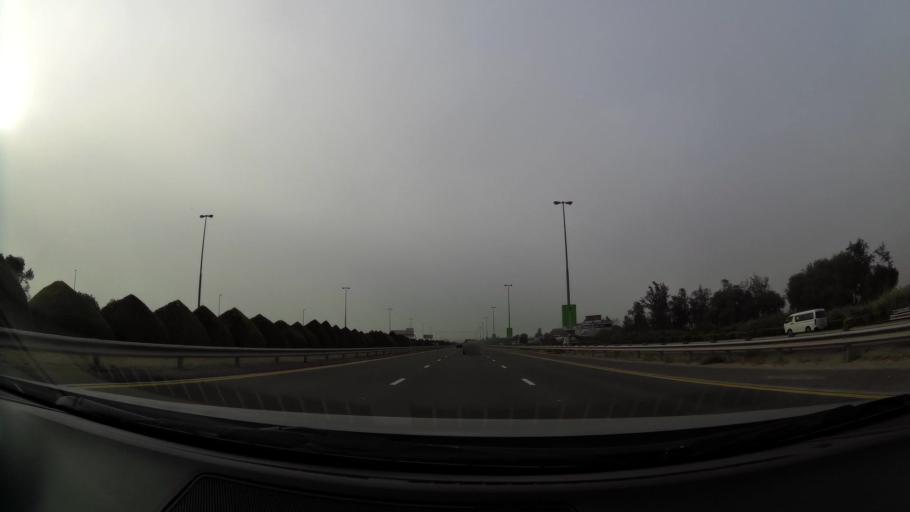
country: AE
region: Dubai
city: Dubai
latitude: 25.1736
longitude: 55.3215
